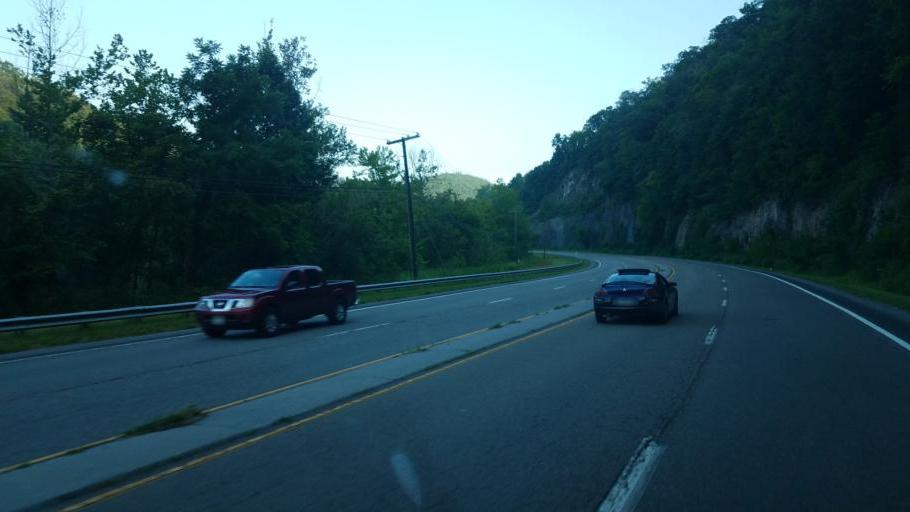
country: US
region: Tennessee
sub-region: Hawkins County
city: Church Hill
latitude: 36.6650
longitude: -82.7534
